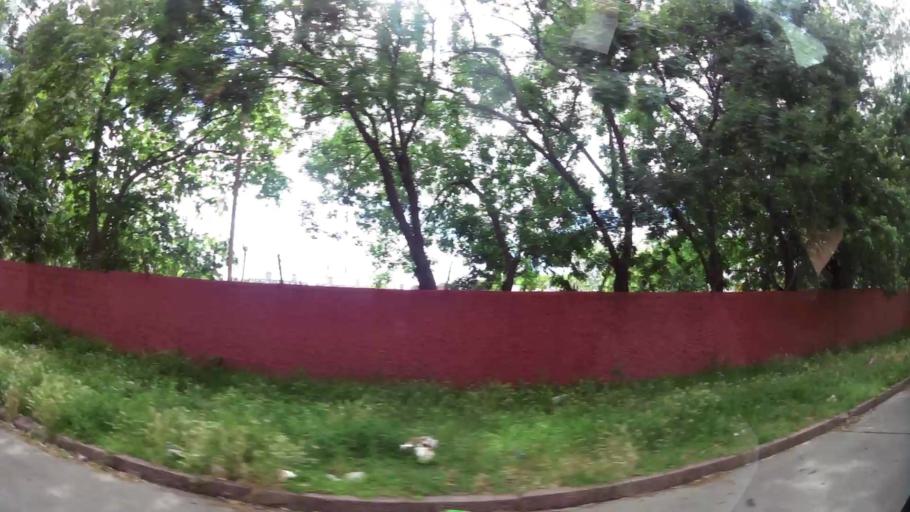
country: UY
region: Montevideo
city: Montevideo
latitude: -34.8795
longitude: -56.1691
